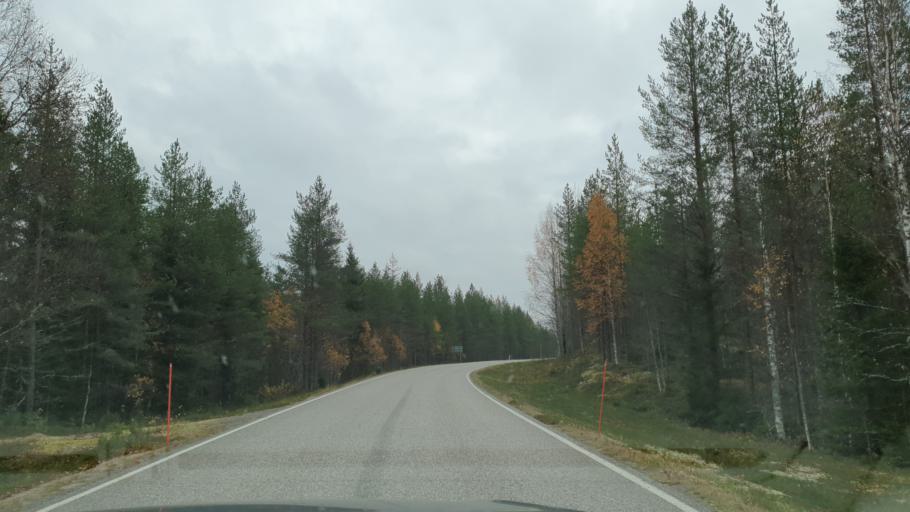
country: FI
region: Kainuu
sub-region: Kajaani
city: Paltamo
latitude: 64.6491
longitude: 27.9644
